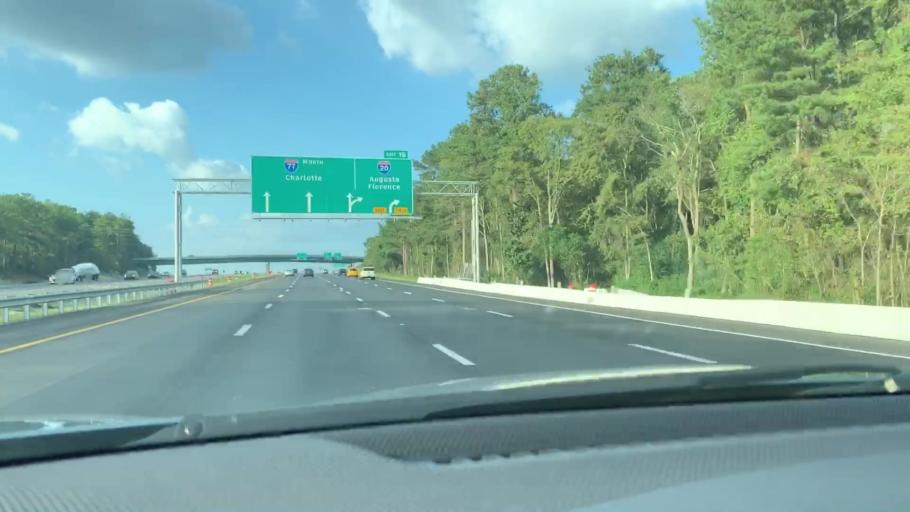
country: US
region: South Carolina
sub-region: Richland County
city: Woodfield
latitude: 34.0605
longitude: -80.9221
